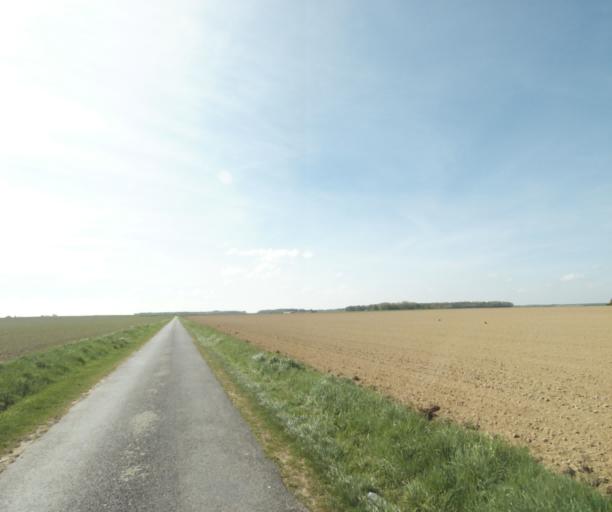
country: FR
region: Ile-de-France
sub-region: Departement de Seine-et-Marne
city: Nangis
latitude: 48.5403
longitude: 3.0372
